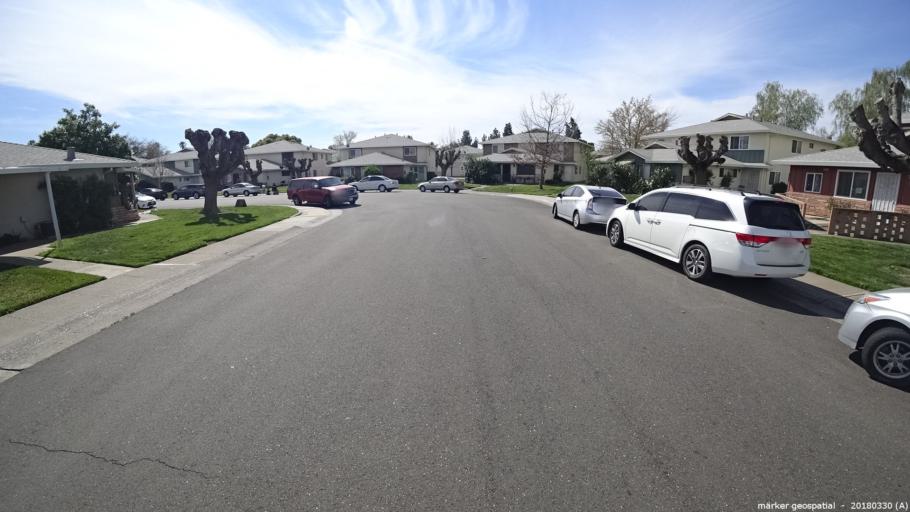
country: US
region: California
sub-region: Sacramento County
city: Rosemont
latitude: 38.5583
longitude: -121.3704
